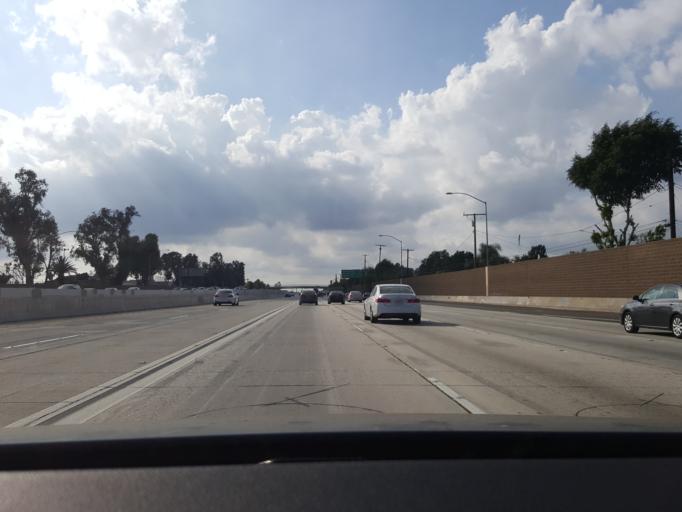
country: US
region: California
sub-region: Los Angeles County
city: Monterey Park
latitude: 34.0719
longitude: -118.1083
